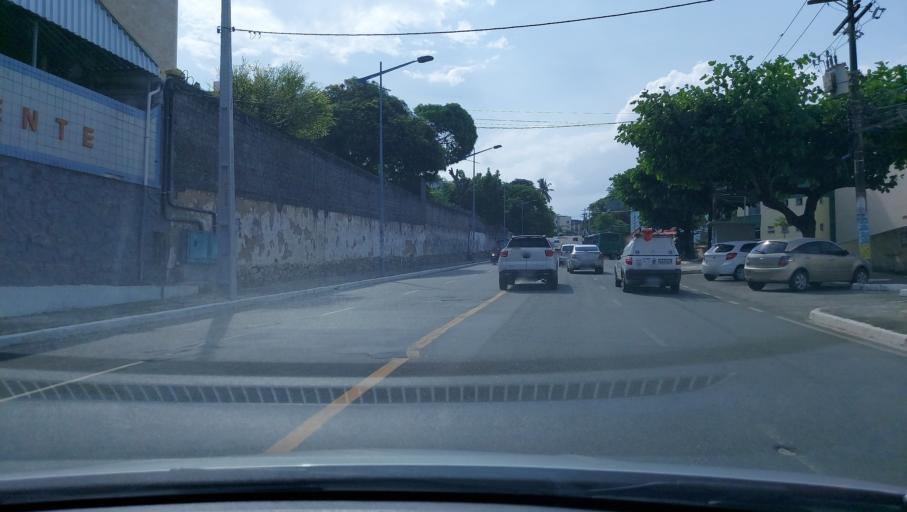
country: BR
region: Bahia
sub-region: Salvador
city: Salvador
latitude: -12.9817
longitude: -38.4436
